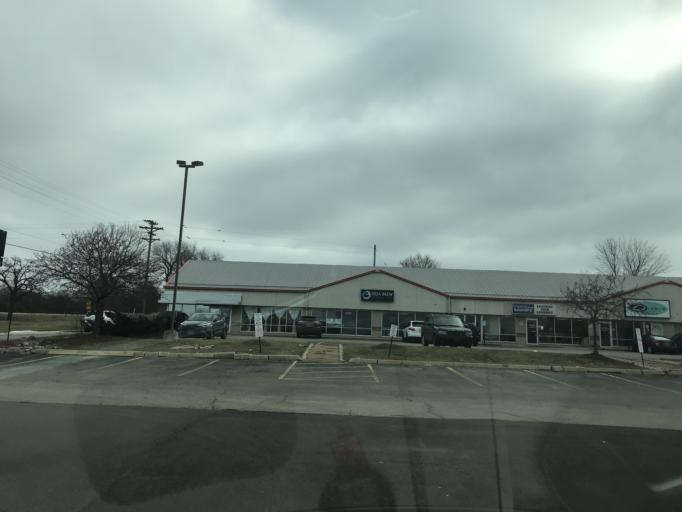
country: US
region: Wisconsin
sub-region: Dane County
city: Monona
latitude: 43.1060
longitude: -89.2976
